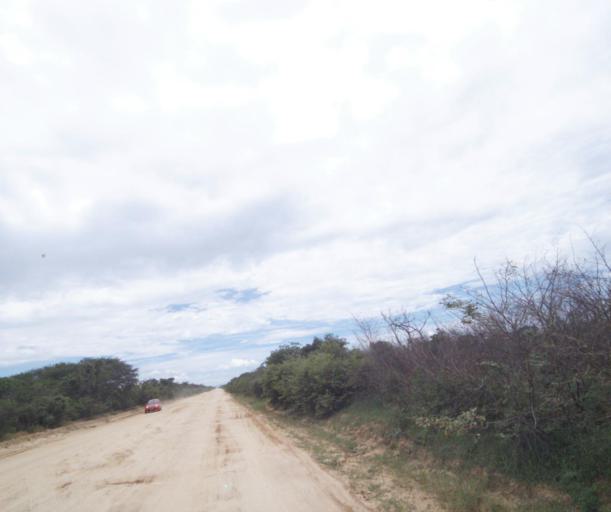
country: BR
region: Bahia
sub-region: Carinhanha
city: Carinhanha
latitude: -14.2390
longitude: -43.8530
